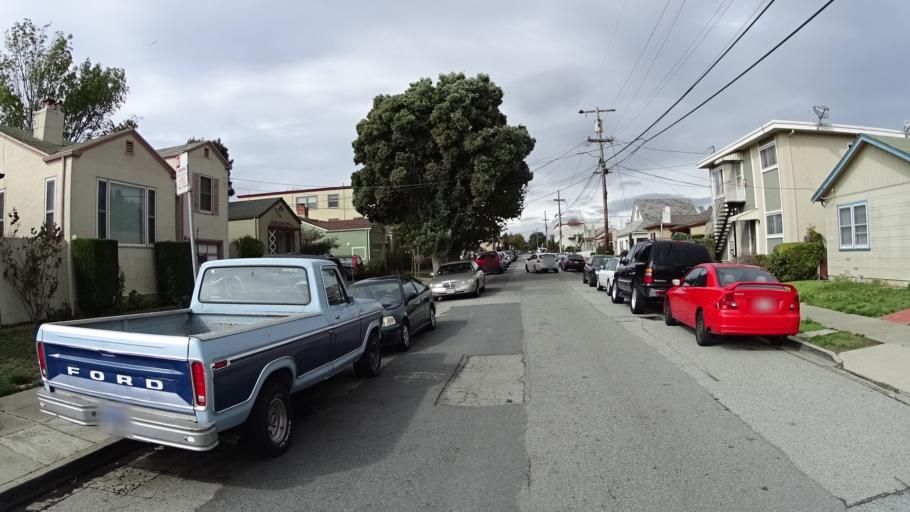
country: US
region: California
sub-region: San Mateo County
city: San Bruno
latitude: 37.6282
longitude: -122.4135
